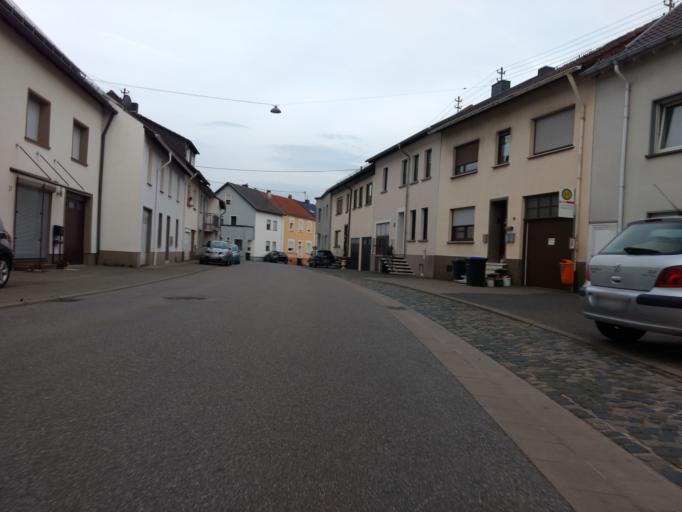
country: DE
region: Saarland
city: Wallerfangen
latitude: 49.3306
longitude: 6.6885
